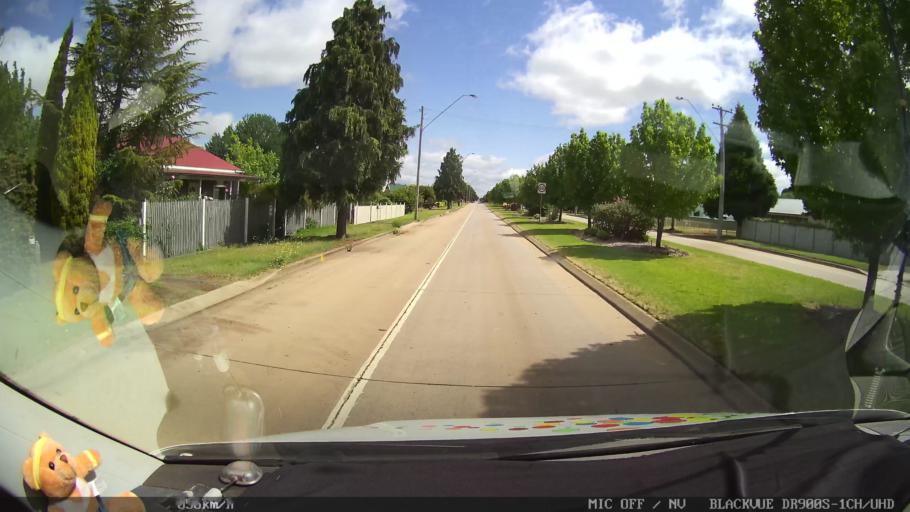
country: AU
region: New South Wales
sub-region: Glen Innes Severn
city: Glen Innes
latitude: -29.7503
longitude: 151.7358
